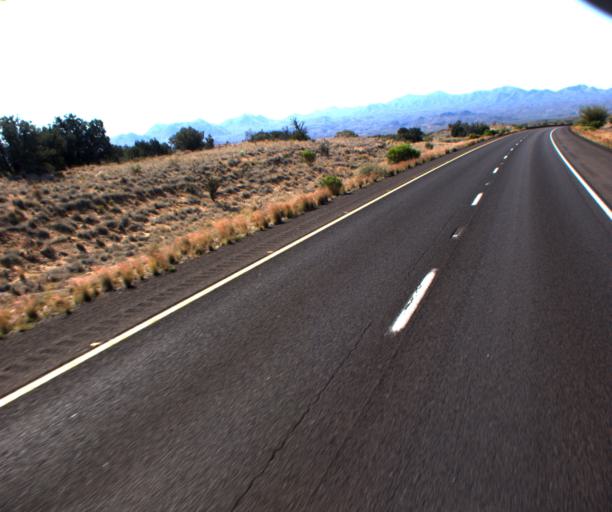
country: US
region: Arizona
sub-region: Mohave County
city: New Kingman-Butler
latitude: 35.1357
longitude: -113.6709
